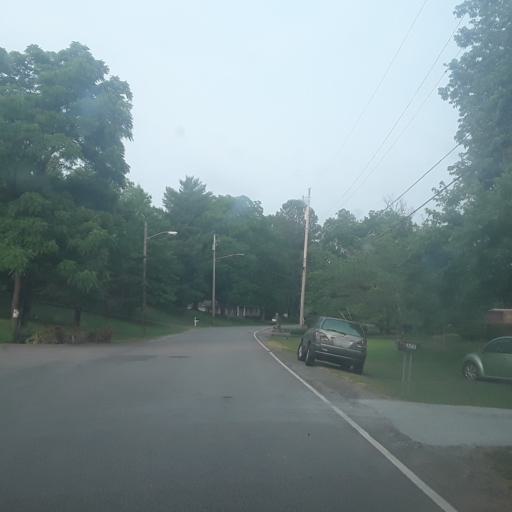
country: US
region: Tennessee
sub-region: Davidson County
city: Oak Hill
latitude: 36.0670
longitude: -86.7526
